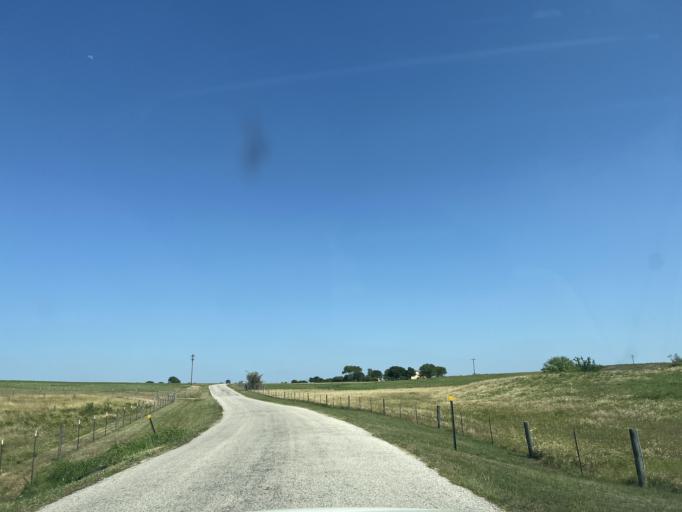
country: US
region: Texas
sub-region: Washington County
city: Brenham
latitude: 30.1693
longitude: -96.3336
